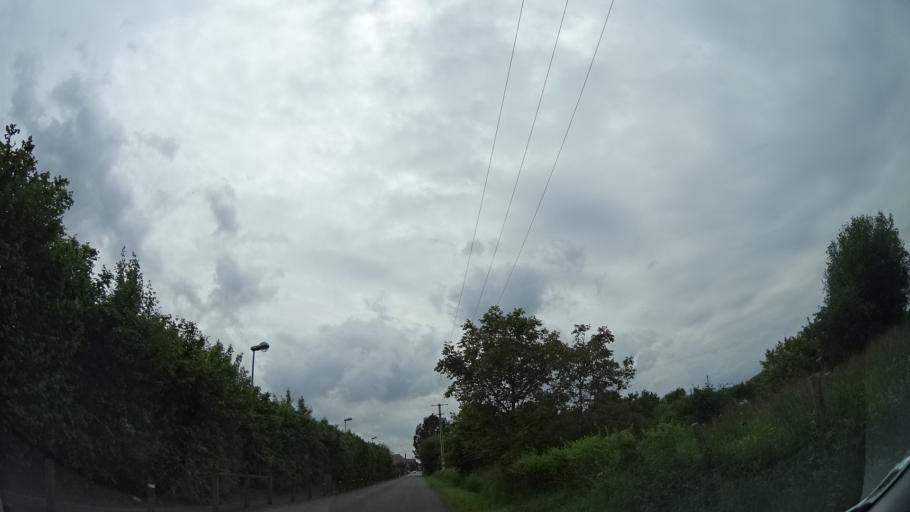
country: FR
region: Brittany
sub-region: Departement d'Ille-et-Vilaine
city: Tinteniac
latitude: 48.2743
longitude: -1.8530
